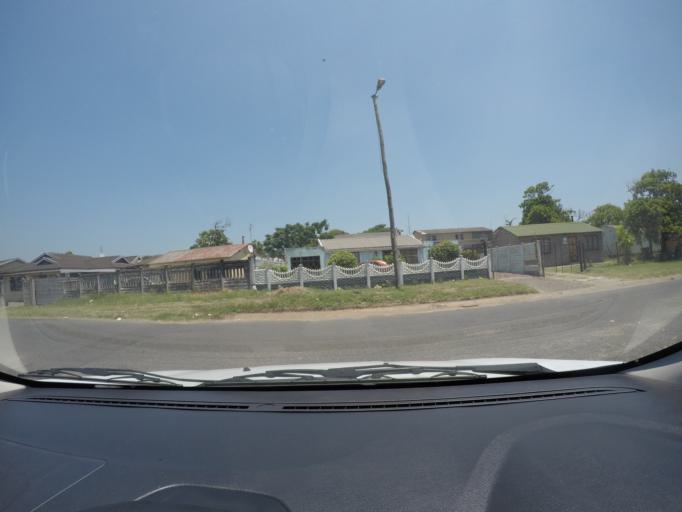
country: ZA
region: KwaZulu-Natal
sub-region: uThungulu District Municipality
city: eSikhawini
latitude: -28.8769
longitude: 31.9097
